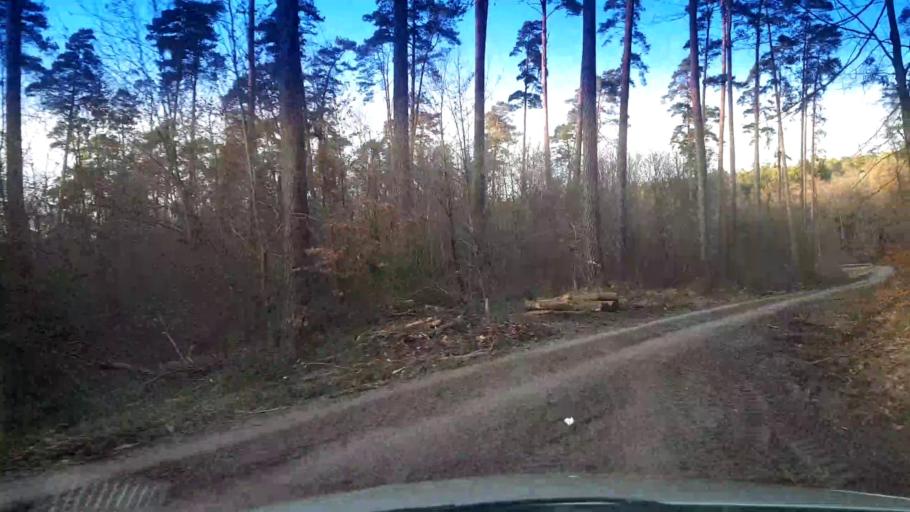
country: DE
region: Bavaria
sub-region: Upper Franconia
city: Strullendorf
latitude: 49.8868
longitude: 10.9707
